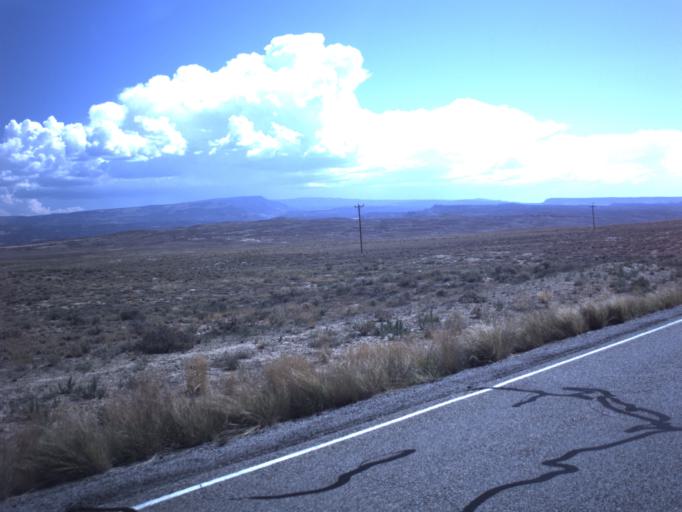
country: US
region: Utah
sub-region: Grand County
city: Moab
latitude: 38.9192
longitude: -109.3334
